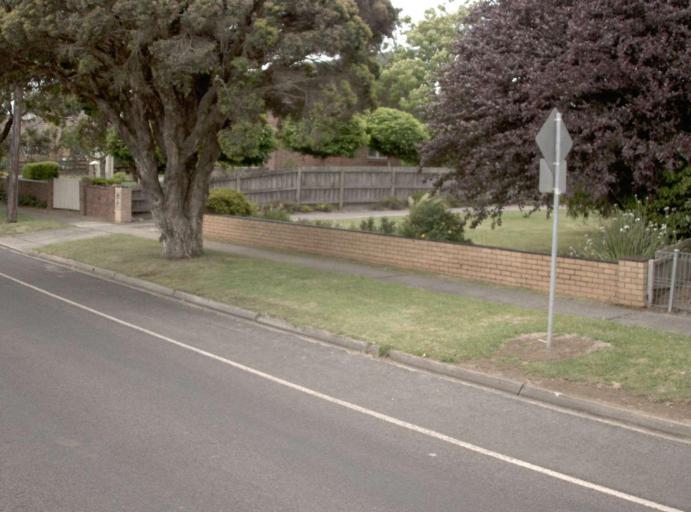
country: AU
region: Victoria
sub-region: Baw Baw
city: Warragul
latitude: -38.1476
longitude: 145.9373
